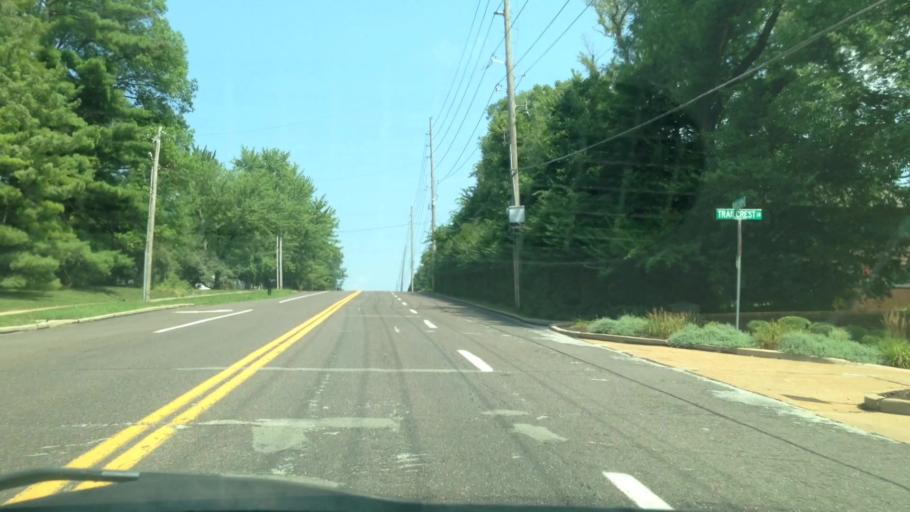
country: US
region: Missouri
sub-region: Saint Louis County
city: Des Peres
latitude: 38.5918
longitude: -90.4441
